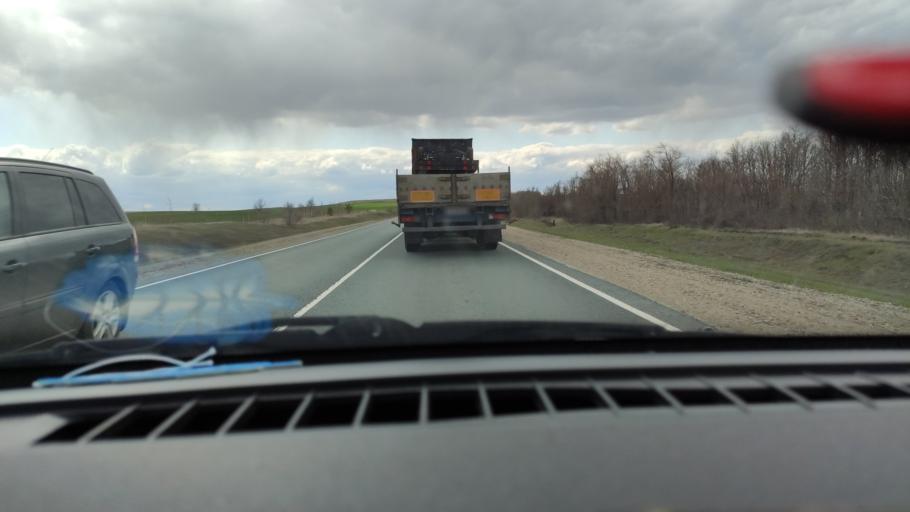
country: RU
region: Saratov
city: Alekseyevka
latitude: 52.2297
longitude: 47.9029
